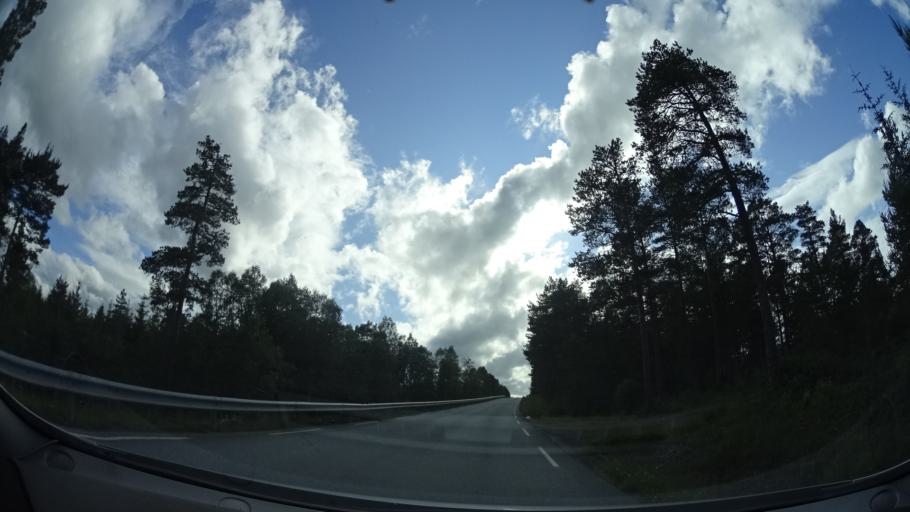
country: NO
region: More og Romsdal
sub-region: Halsa
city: Liaboen
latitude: 63.1275
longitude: 8.3737
